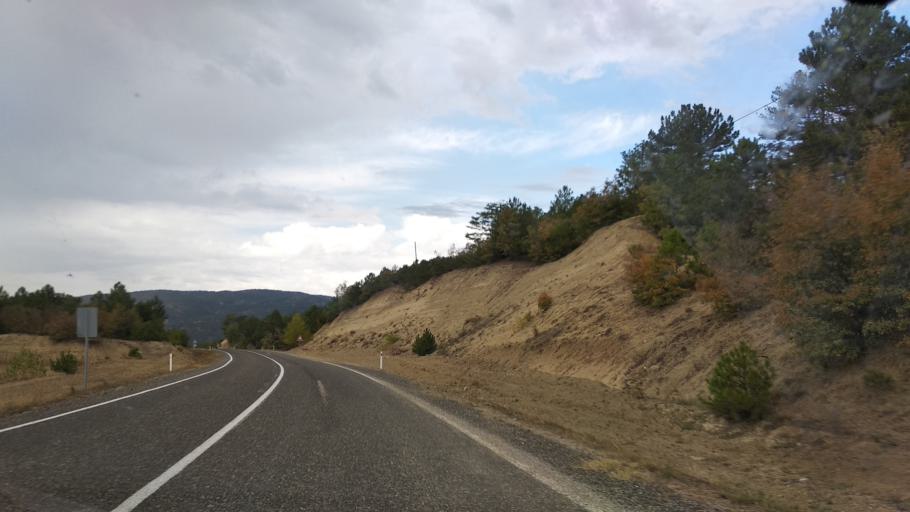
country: TR
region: Bolu
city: Seben
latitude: 40.3367
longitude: 31.4366
